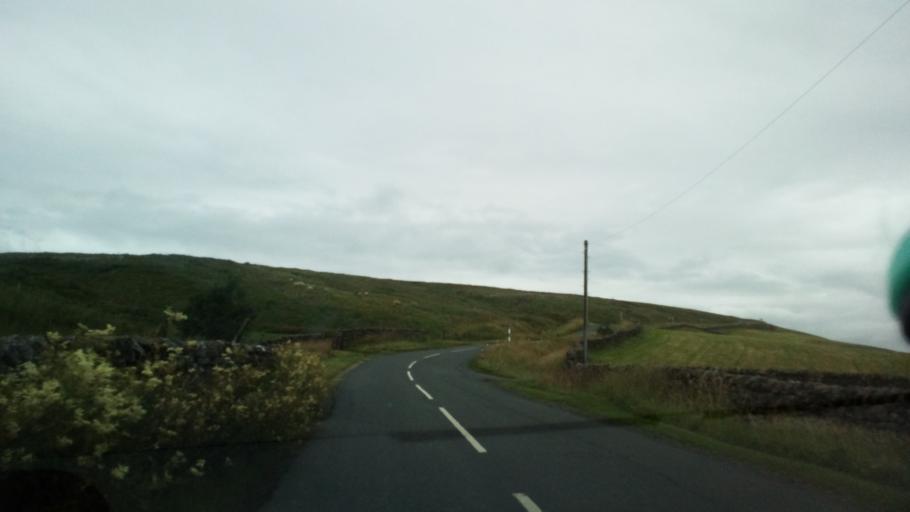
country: GB
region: England
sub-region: County Durham
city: Holwick
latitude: 54.5826
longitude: -2.2050
